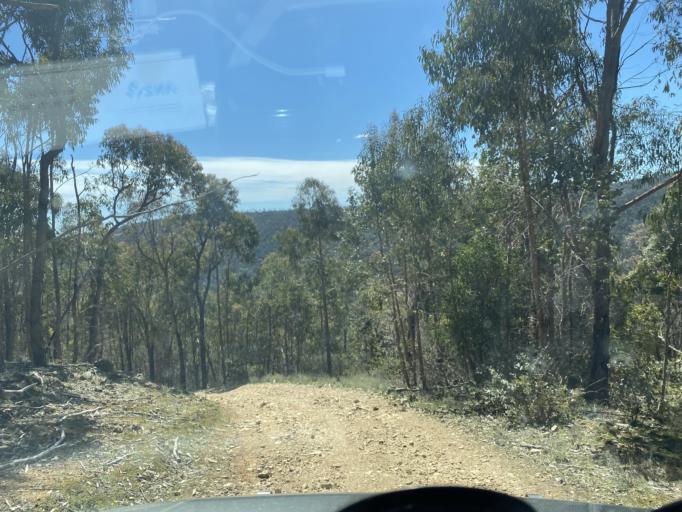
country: AU
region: Victoria
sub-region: Benalla
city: Benalla
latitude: -36.7209
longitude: 146.1823
